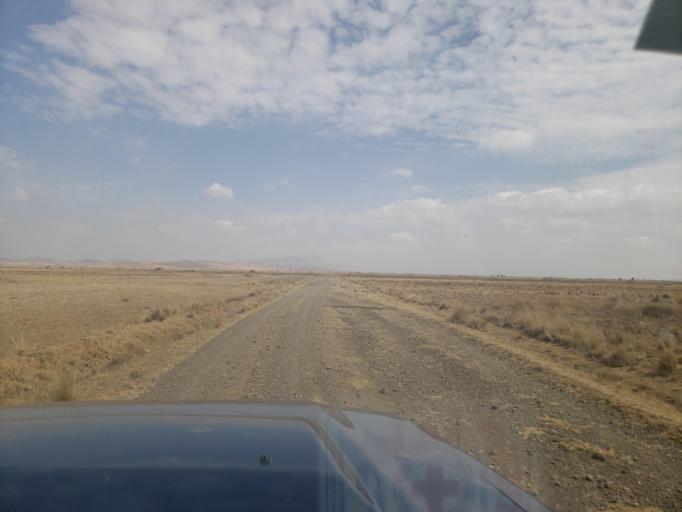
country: BO
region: La Paz
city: Batallas
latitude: -16.4140
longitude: -68.4305
